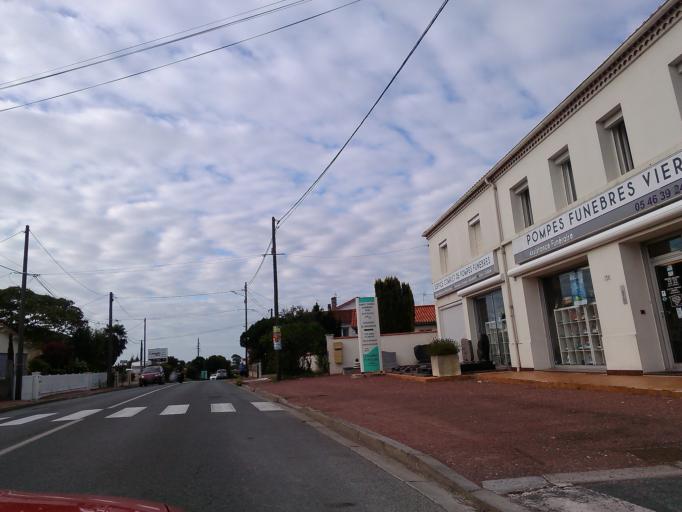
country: FR
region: Poitou-Charentes
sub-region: Departement de la Charente-Maritime
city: Royan
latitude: 45.6424
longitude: -1.0249
